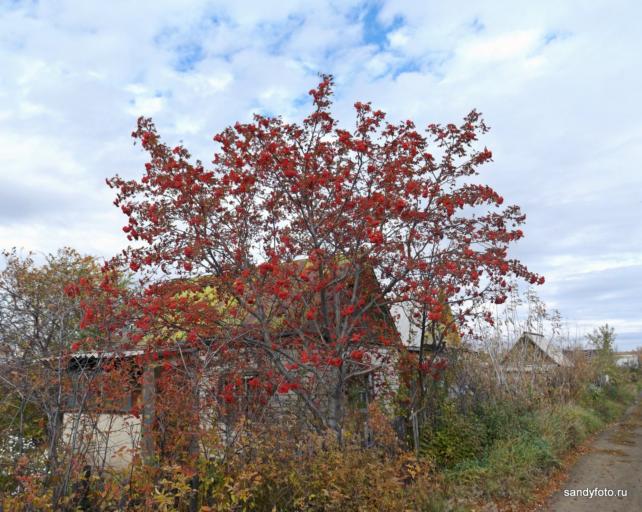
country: RU
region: Chelyabinsk
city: Troitsk
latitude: 54.0650
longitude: 61.6242
